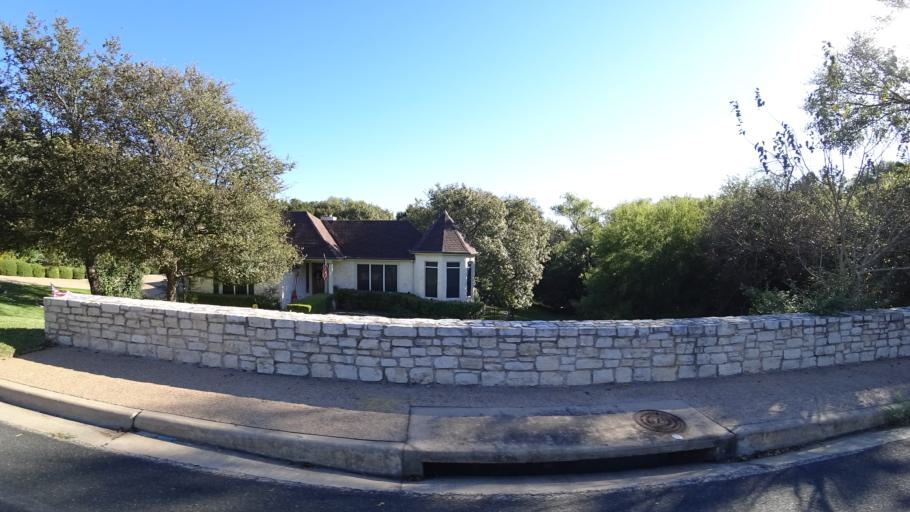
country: US
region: Texas
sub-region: Travis County
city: West Lake Hills
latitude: 30.3330
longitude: -97.8044
